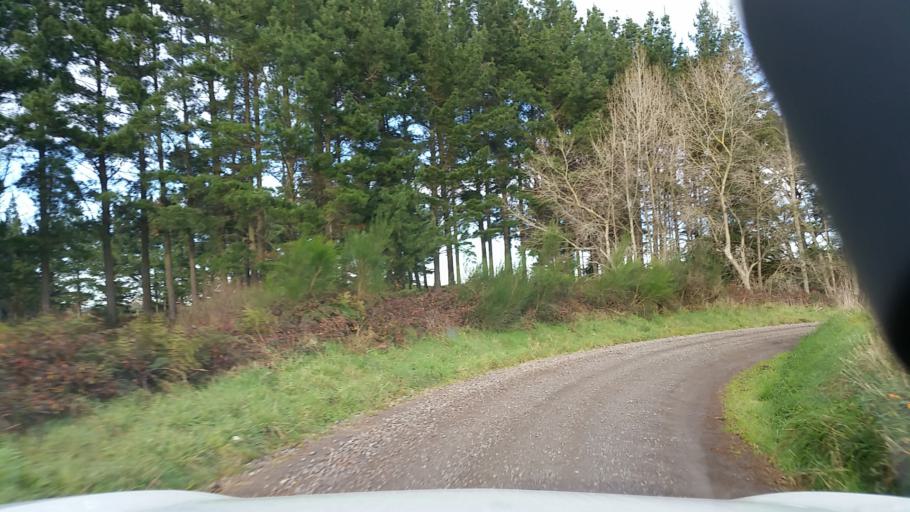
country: NZ
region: Bay of Plenty
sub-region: Rotorua District
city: Rotorua
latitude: -38.2682
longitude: 176.1568
